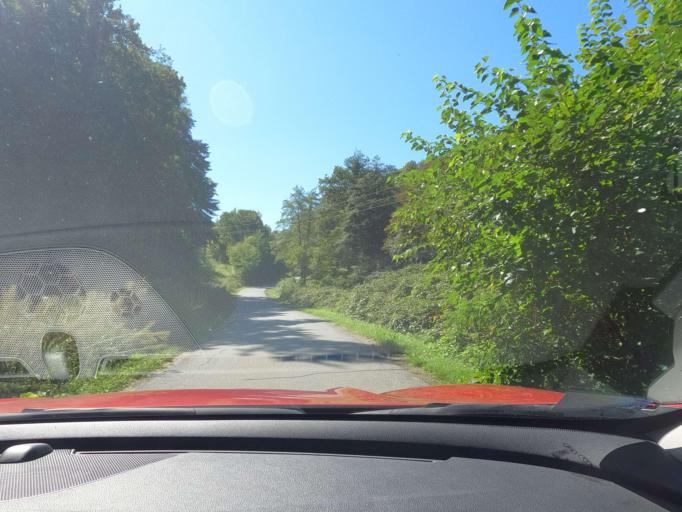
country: HR
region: Sisacko-Moslavacka
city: Petrinja
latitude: 45.4052
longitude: 16.2473
